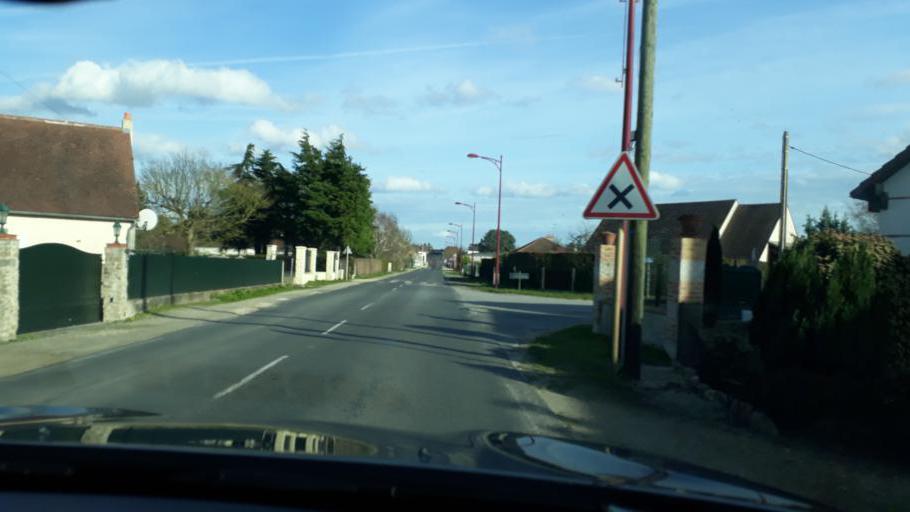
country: FR
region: Centre
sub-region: Departement du Loiret
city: Chilleurs-aux-Bois
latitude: 48.0708
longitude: 2.1278
